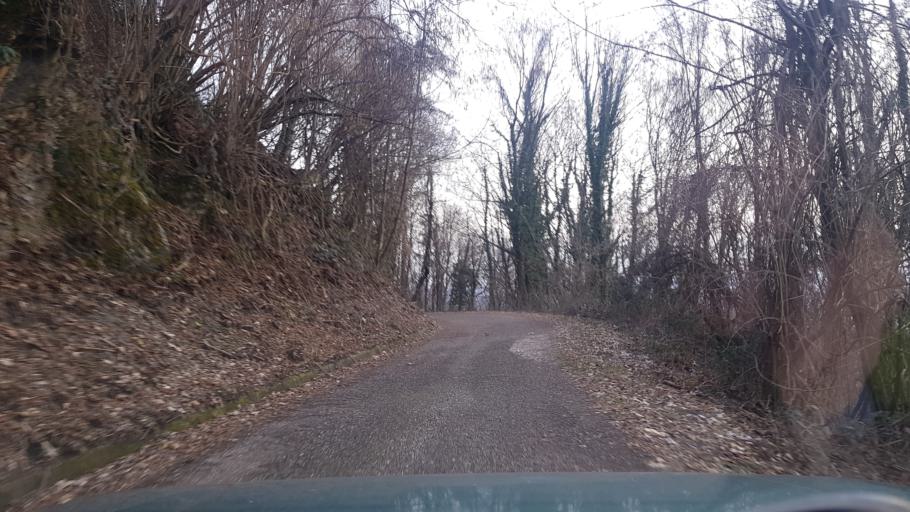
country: IT
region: Friuli Venezia Giulia
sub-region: Provincia di Udine
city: Torreano
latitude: 46.1605
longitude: 13.4444
